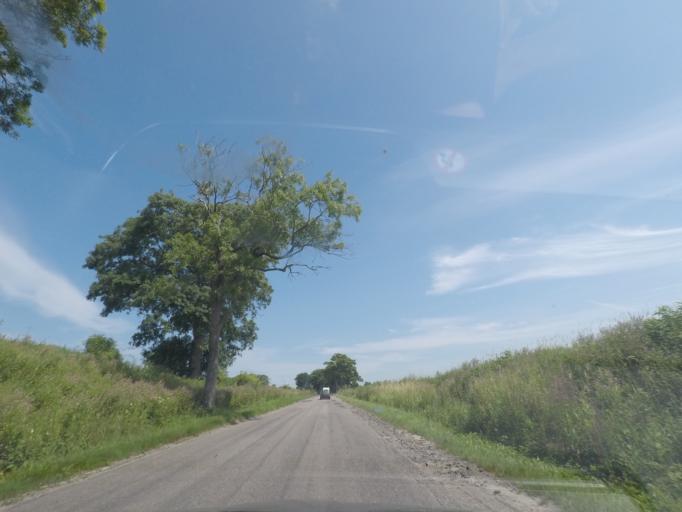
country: PL
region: West Pomeranian Voivodeship
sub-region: Powiat slawienski
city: Darlowo
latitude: 54.4527
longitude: 16.4839
